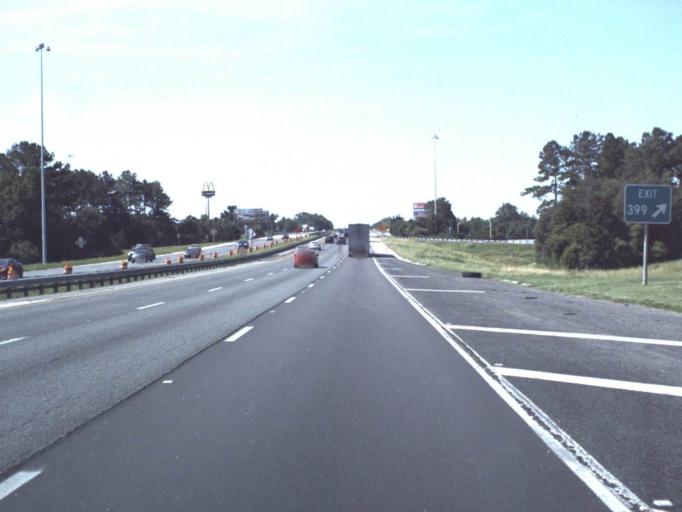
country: US
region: Florida
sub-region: Alachua County
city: High Springs
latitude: 29.8052
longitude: -82.5136
